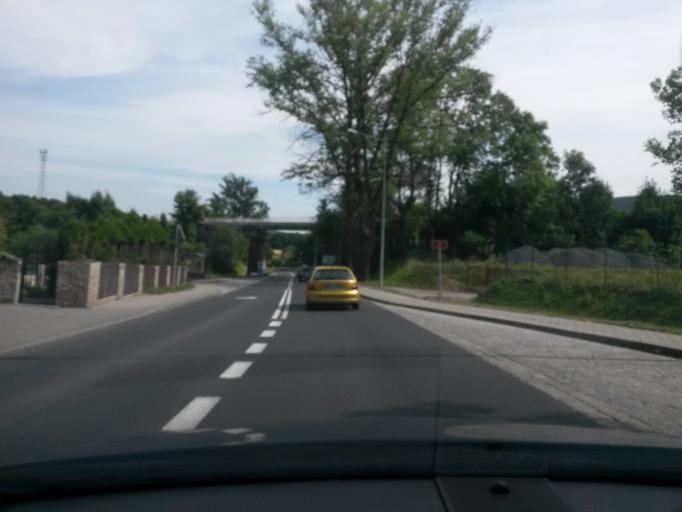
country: PL
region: Lower Silesian Voivodeship
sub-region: Powiat jeleniogorski
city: Janowice Wielkie
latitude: 50.9093
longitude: 15.9587
